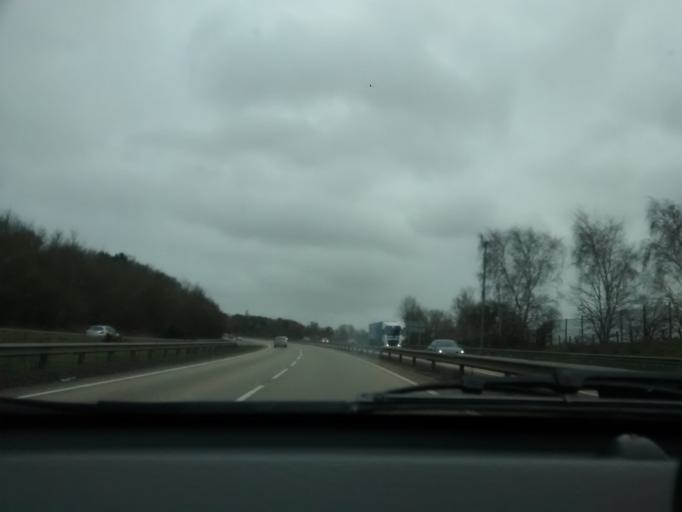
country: GB
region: England
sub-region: Suffolk
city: Bramford
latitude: 52.0854
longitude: 1.1119
